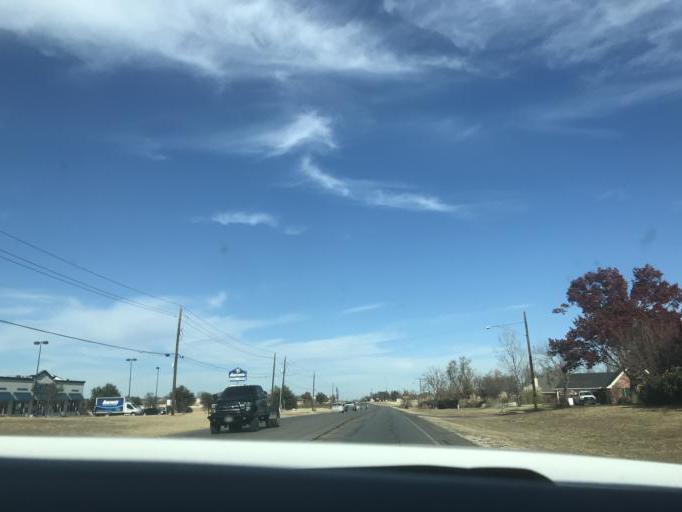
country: US
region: Texas
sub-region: Erath County
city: Stephenville
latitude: 32.2143
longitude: -98.2431
